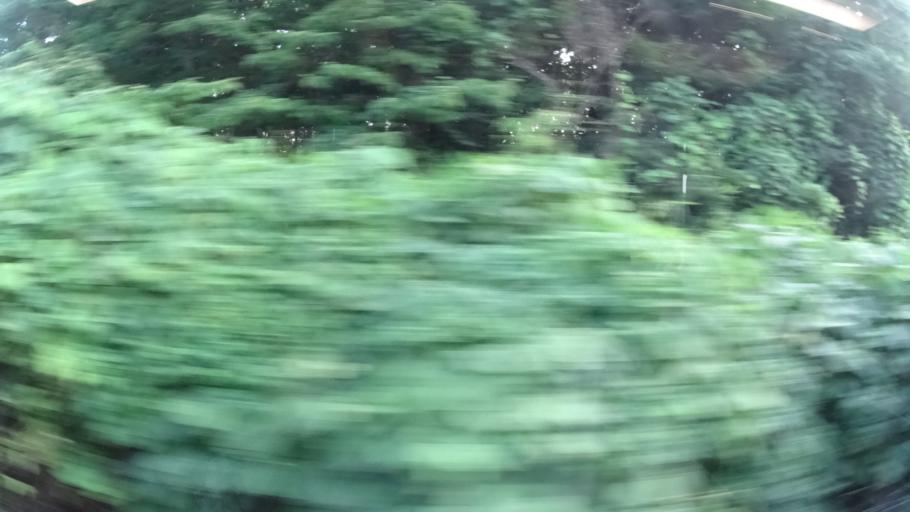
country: JP
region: Ibaraki
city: Mito-shi
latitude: 36.3804
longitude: 140.4446
